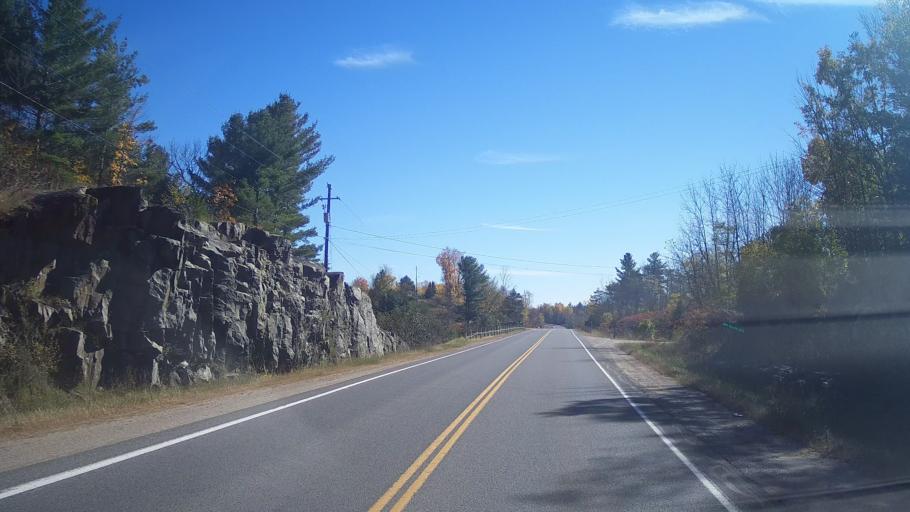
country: CA
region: Ontario
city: Skatepark
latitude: 44.6274
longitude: -76.7025
